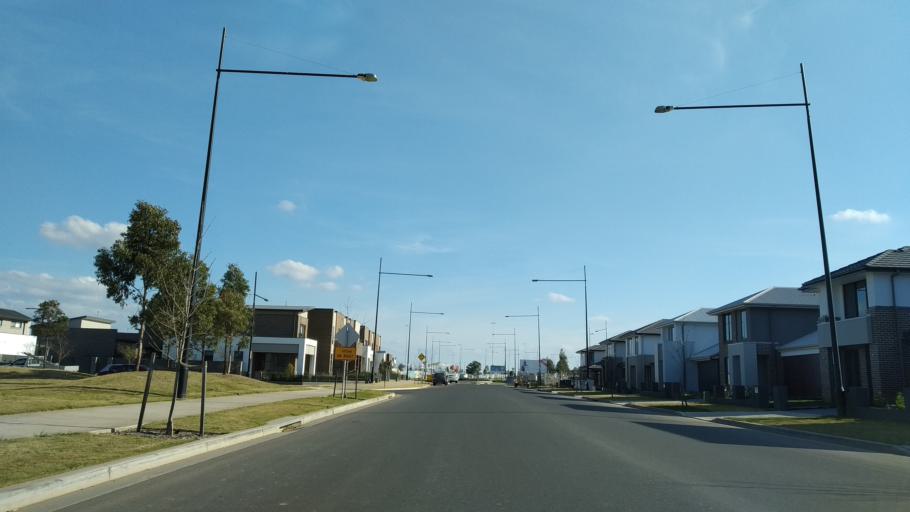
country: AU
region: New South Wales
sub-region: Blacktown
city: Hassall Grove
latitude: -33.6938
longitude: 150.8221
